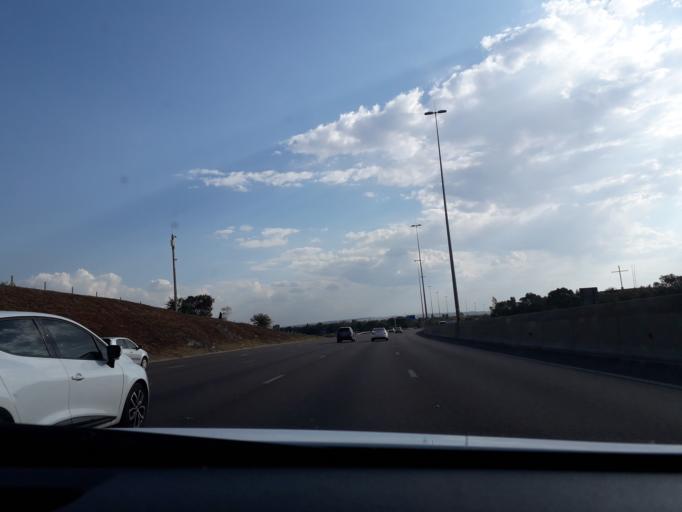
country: ZA
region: Gauteng
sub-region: City of Tshwane Metropolitan Municipality
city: Centurion
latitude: -25.8543
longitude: 28.2258
